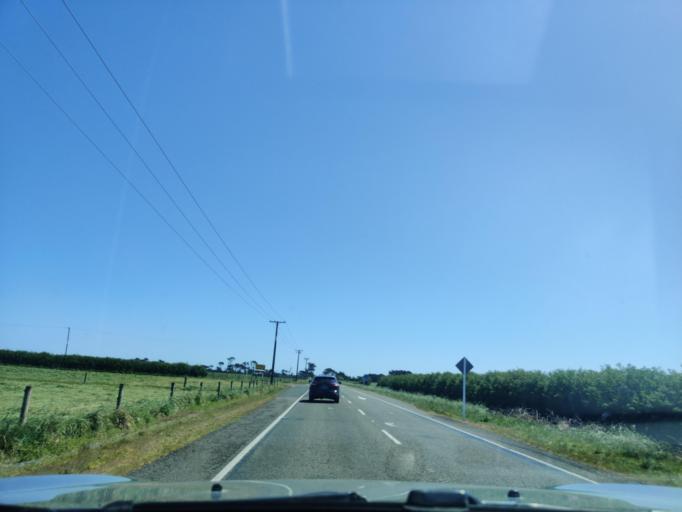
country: NZ
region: Taranaki
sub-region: South Taranaki District
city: Hawera
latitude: -39.5461
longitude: 174.0799
